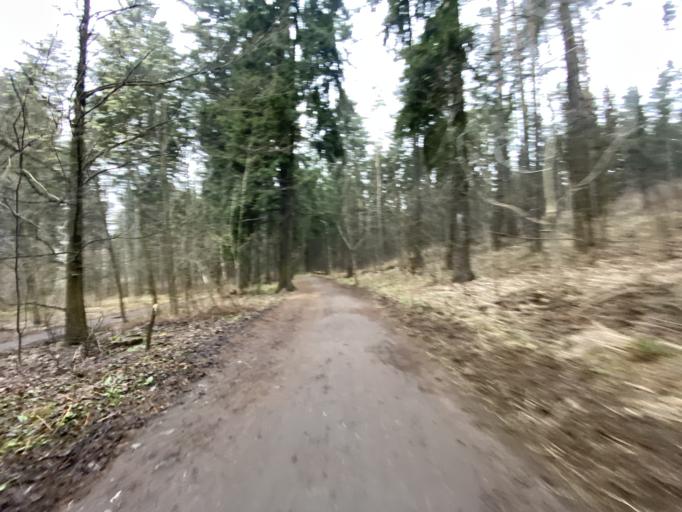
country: BY
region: Minsk
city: Borovlyany
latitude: 53.9454
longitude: 27.6578
